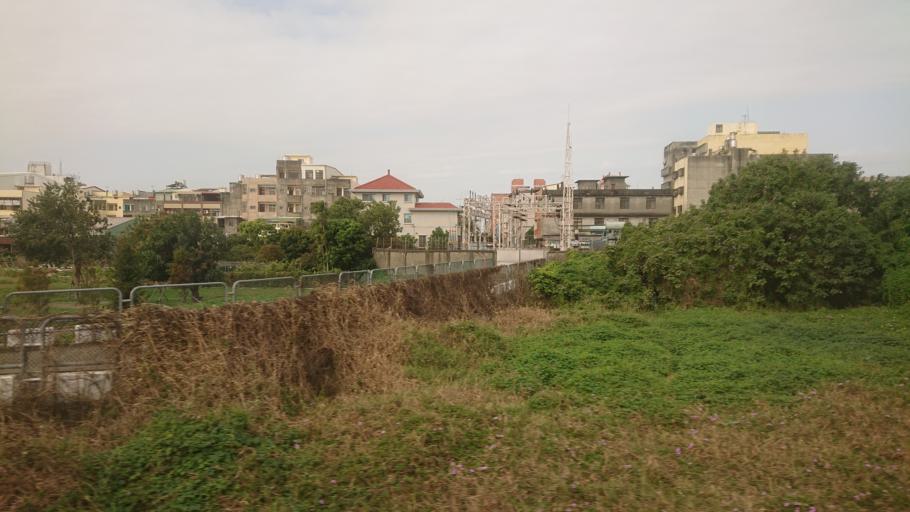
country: TW
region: Taiwan
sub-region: Changhua
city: Chang-hua
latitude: 24.0685
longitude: 120.5330
